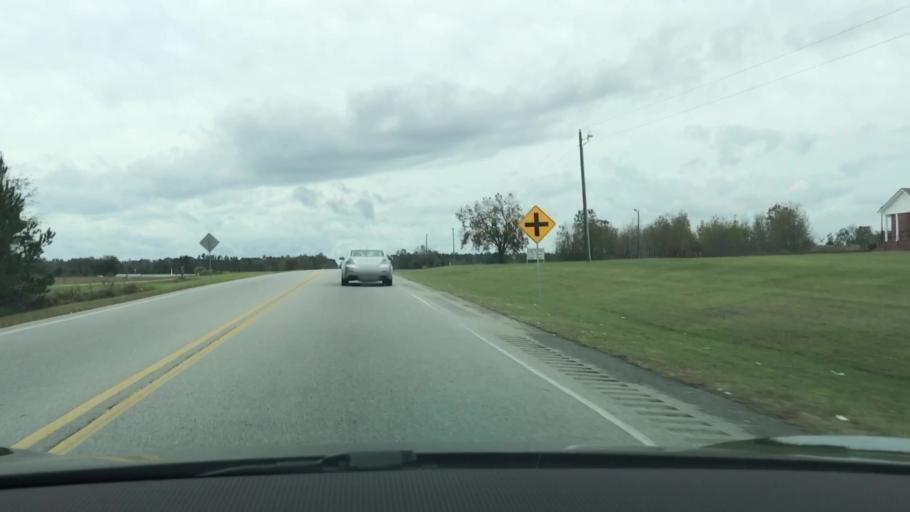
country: US
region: Georgia
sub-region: Jefferson County
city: Louisville
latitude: 32.9497
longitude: -82.3946
